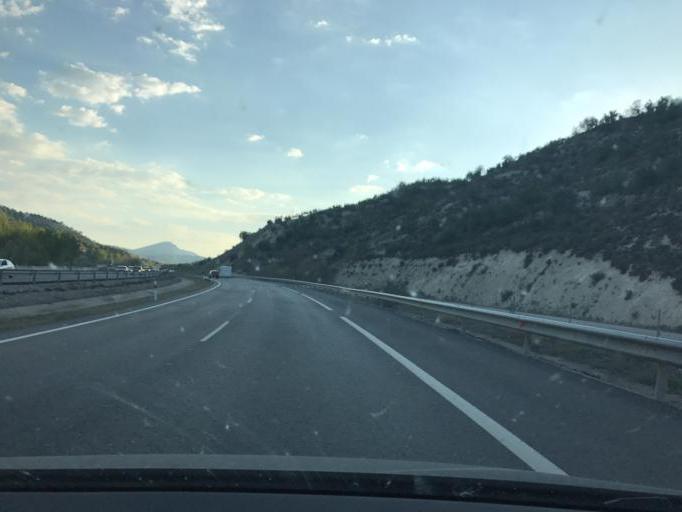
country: ES
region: Andalusia
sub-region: Provincia de Jaen
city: Campillo de Arenas
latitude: 37.5721
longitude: -3.6139
